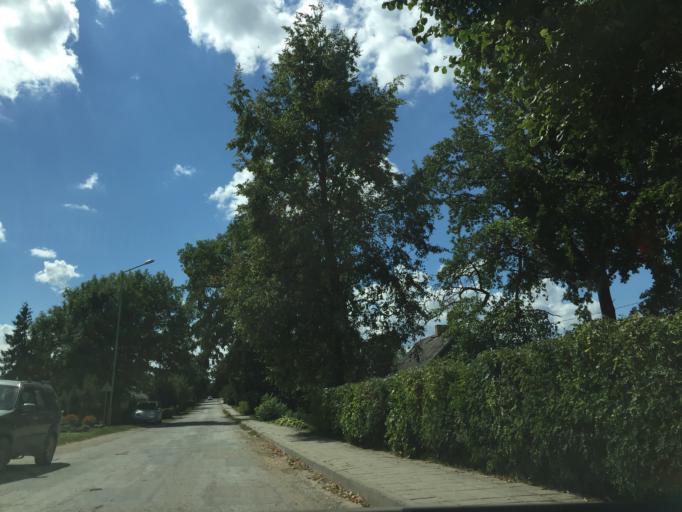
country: LV
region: Rundales
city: Pilsrundale
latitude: 56.2758
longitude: 24.0006
